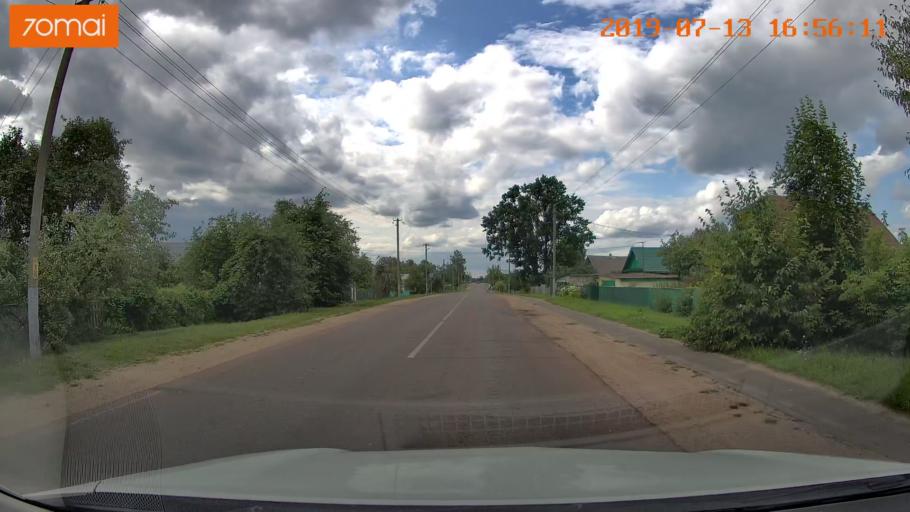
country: BY
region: Mogilev
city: Kirawsk
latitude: 53.2718
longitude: 29.4610
